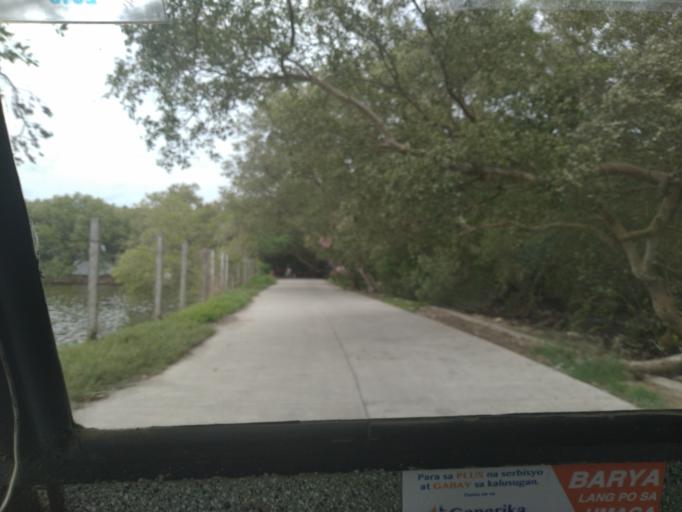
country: PH
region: Central Visayas
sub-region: Province of Negros Oriental
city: Okiot
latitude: 9.5463
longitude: 123.1536
